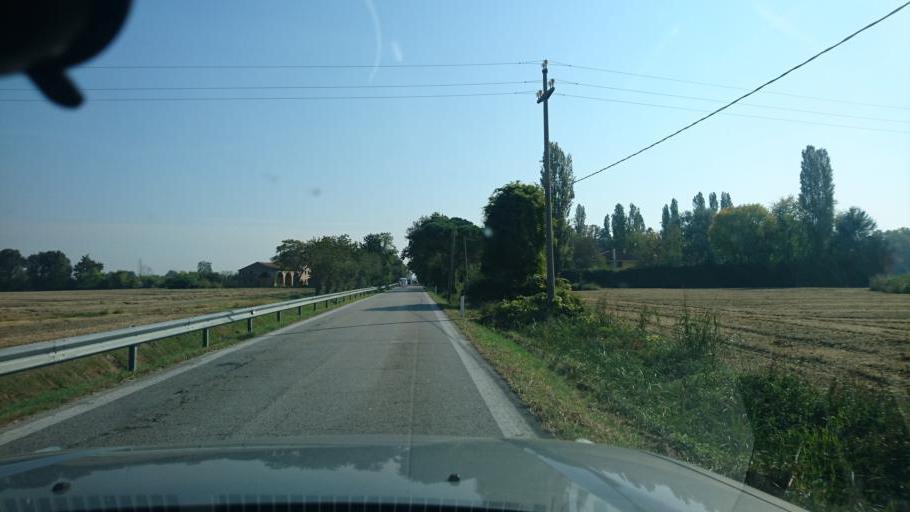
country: IT
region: Veneto
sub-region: Provincia di Padova
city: Rubano
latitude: 45.4198
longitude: 11.7779
